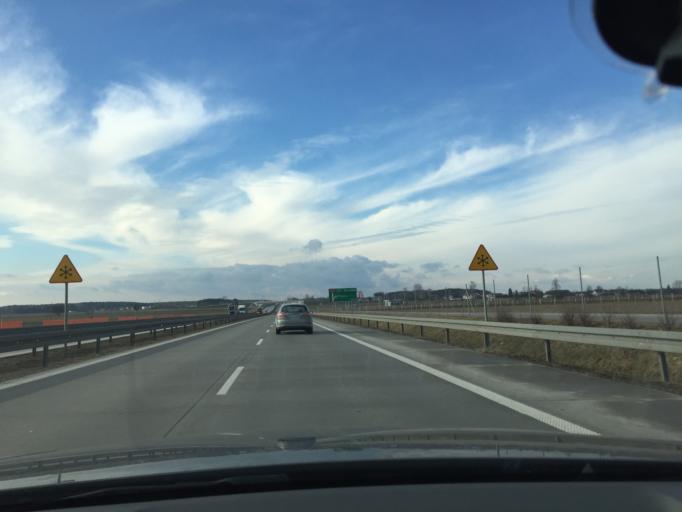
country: PL
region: Lodz Voivodeship
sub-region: Powiat piotrkowski
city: Wolborz
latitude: 51.4800
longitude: 19.8110
